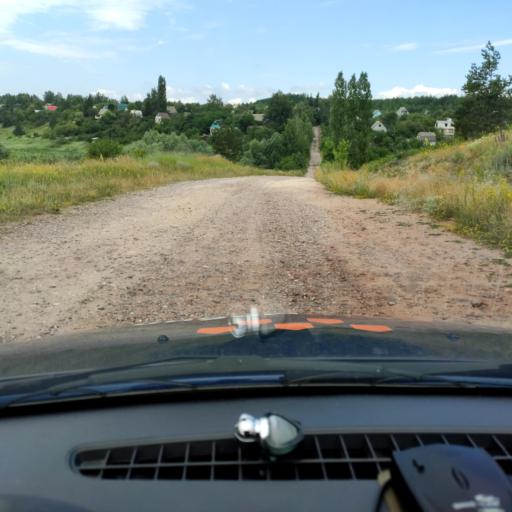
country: RU
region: Voronezj
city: Ramon'
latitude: 52.0743
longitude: 39.3197
